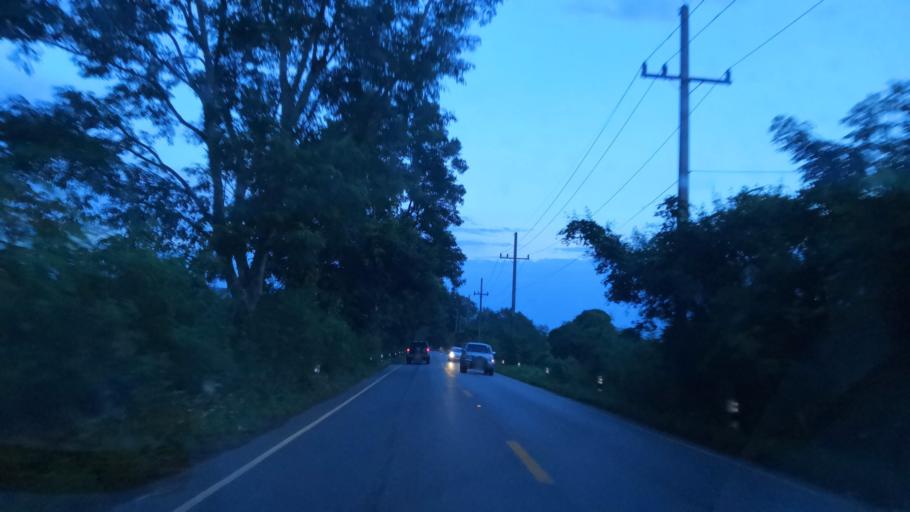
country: TH
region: Chiang Rai
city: Wiang Chiang Rung
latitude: 19.9729
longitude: 99.9774
